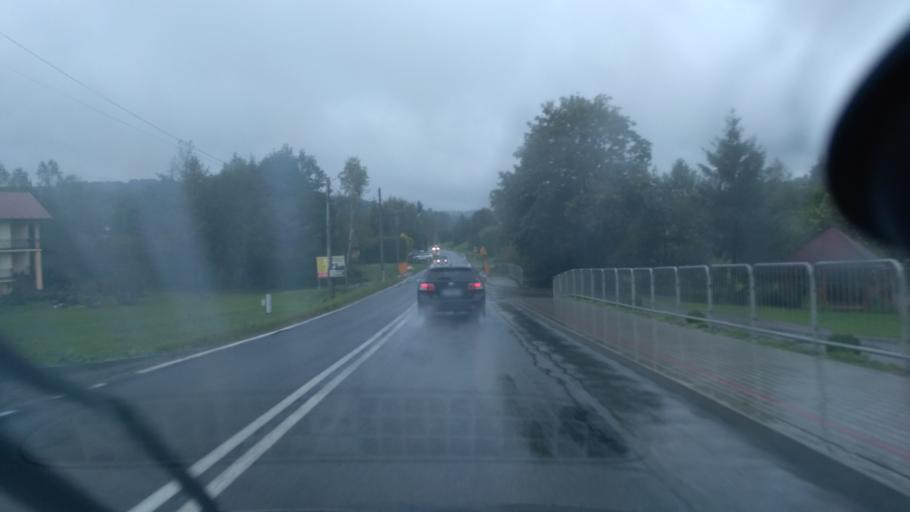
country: PL
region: Subcarpathian Voivodeship
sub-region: Powiat ropczycko-sedziszowski
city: Niedzwiada
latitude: 50.0038
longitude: 21.5585
